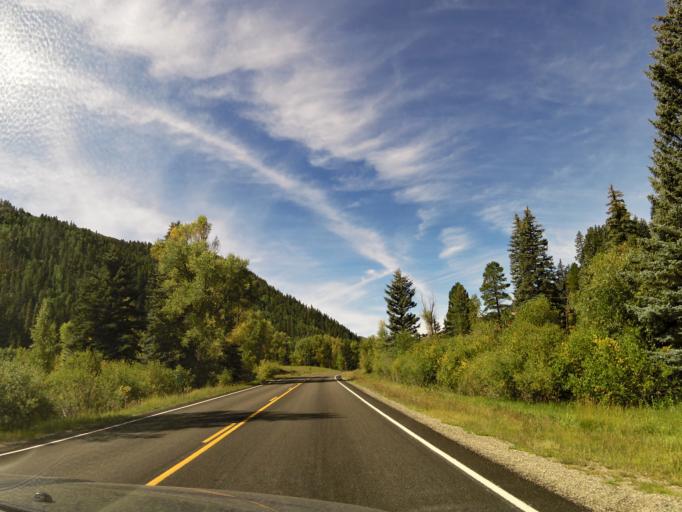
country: US
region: Colorado
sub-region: Montezuma County
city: Mancos
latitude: 37.6101
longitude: -108.0903
